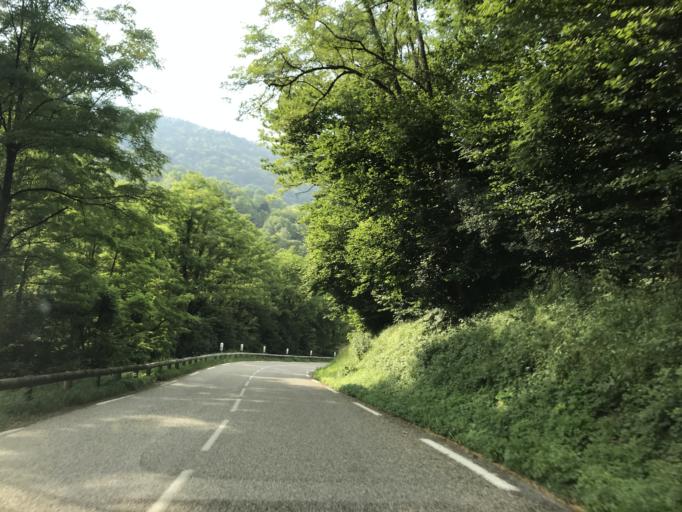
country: FR
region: Rhone-Alpes
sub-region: Departement de l'Isere
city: Allevard
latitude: 45.4107
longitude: 6.0865
